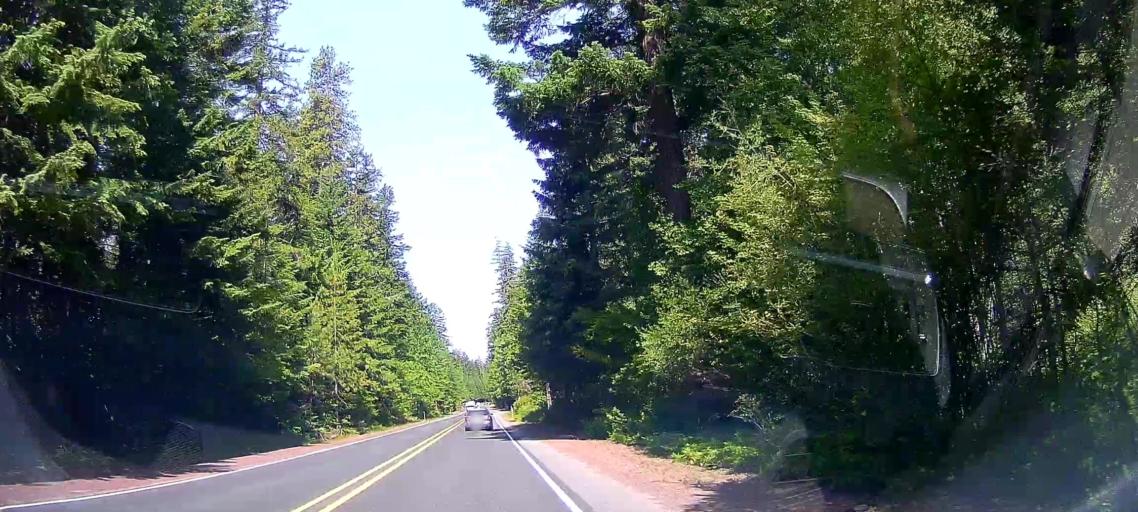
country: US
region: Oregon
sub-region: Jefferson County
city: Warm Springs
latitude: 45.1142
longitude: -121.5710
